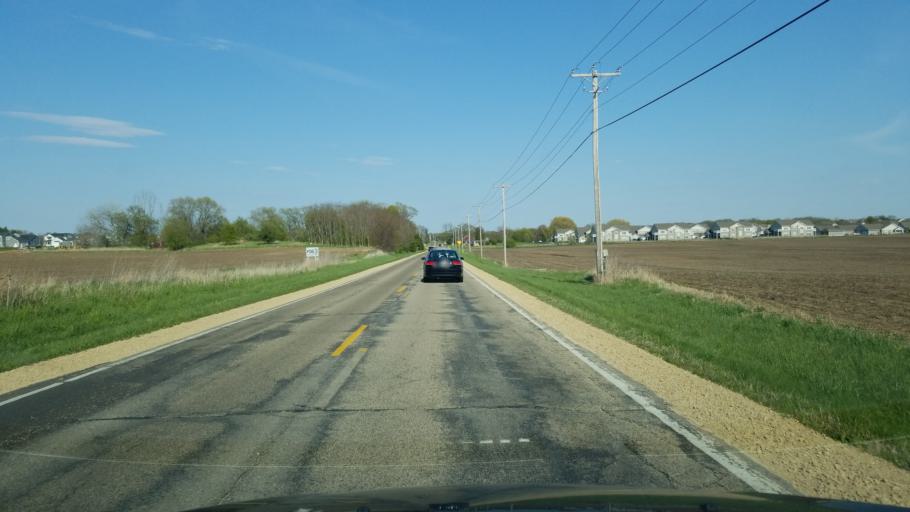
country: US
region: Wisconsin
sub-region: Dane County
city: Oregon
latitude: 42.9291
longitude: -89.4131
